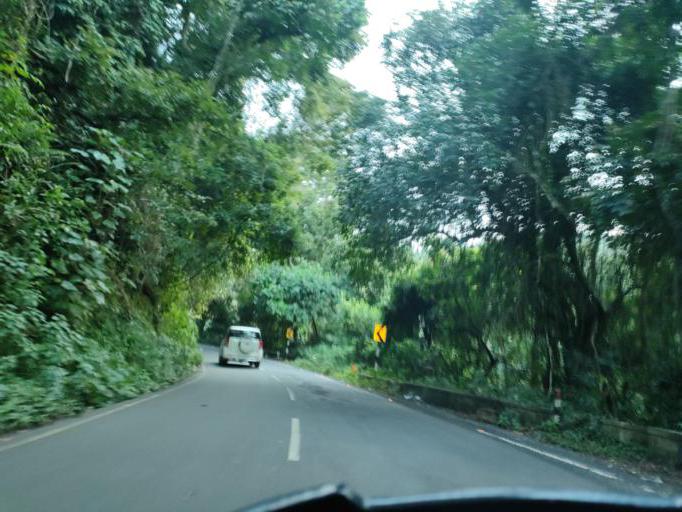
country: IN
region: Tamil Nadu
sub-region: Dindigul
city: Kodaikanal
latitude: 10.2543
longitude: 77.5250
